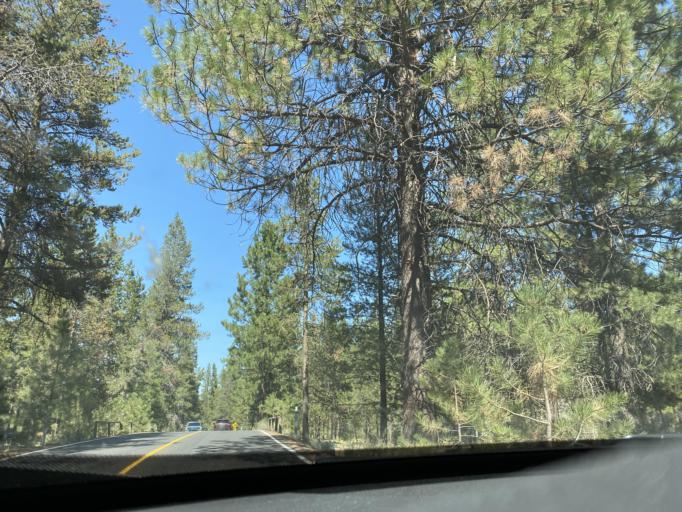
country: US
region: Oregon
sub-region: Deschutes County
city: Sunriver
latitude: 43.8898
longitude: -121.4286
